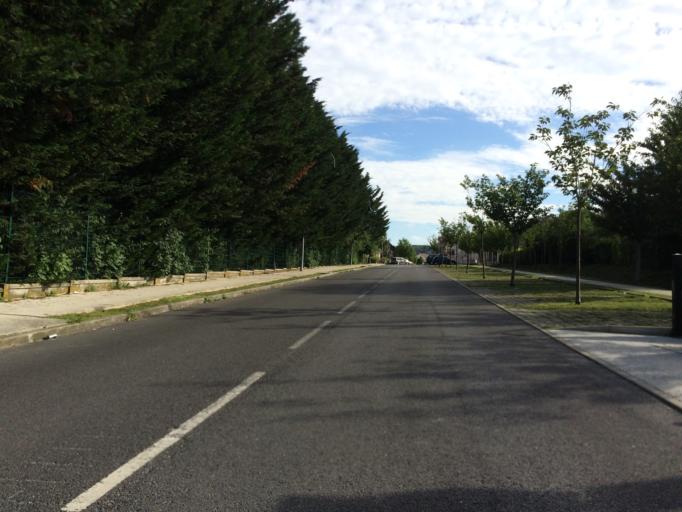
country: FR
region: Ile-de-France
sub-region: Departement de l'Essonne
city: Saulx-les-Chartreux
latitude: 48.6906
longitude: 2.2784
